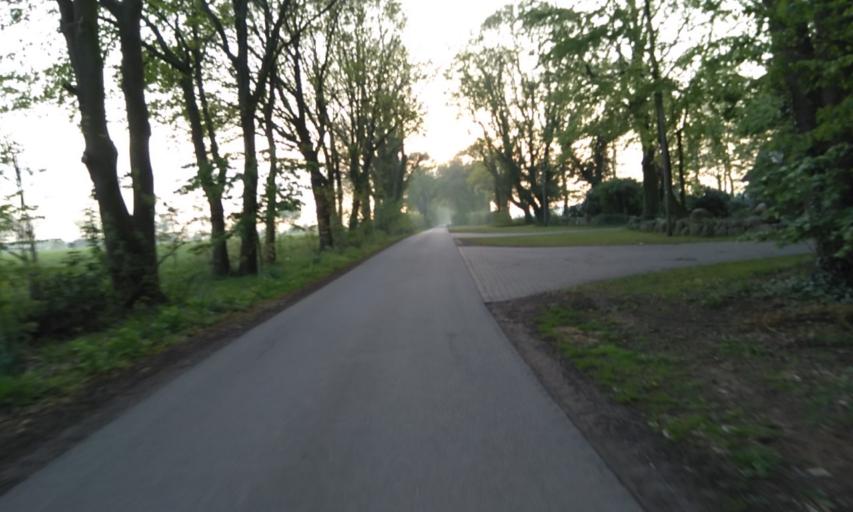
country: DE
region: Lower Saxony
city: Bargstedt
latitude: 53.4972
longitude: 9.4344
